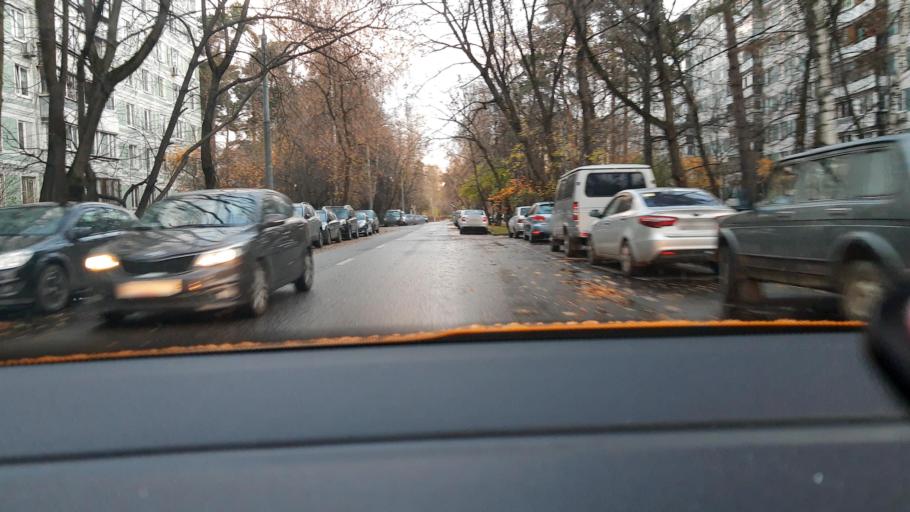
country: RU
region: Moscow
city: Vatutino
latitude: 55.8855
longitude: 37.6962
